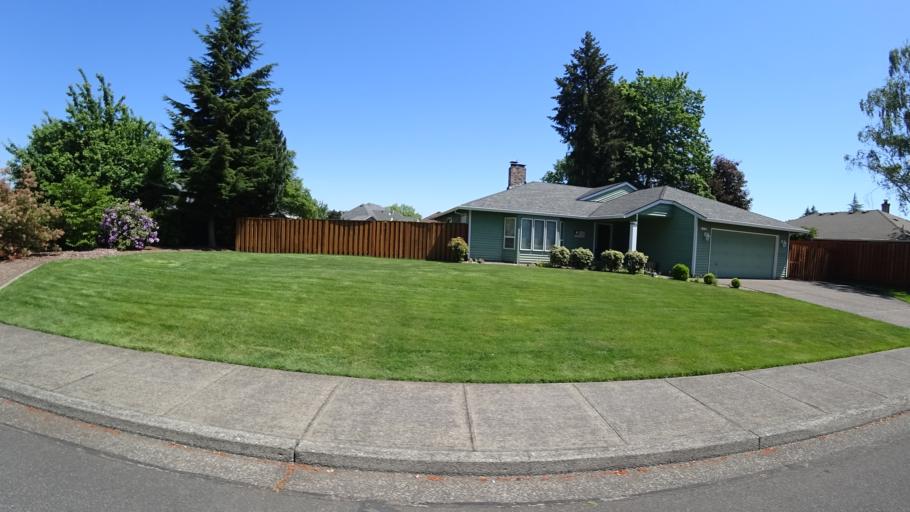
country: US
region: Oregon
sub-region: Washington County
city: Rockcreek
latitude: 45.5365
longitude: -122.9235
